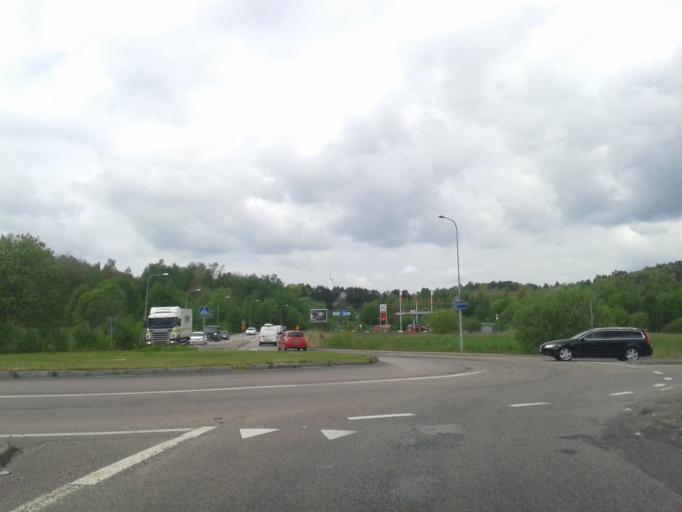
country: SE
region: Vaestra Goetaland
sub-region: Goteborg
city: Hammarkullen
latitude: 57.7882
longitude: 12.0452
